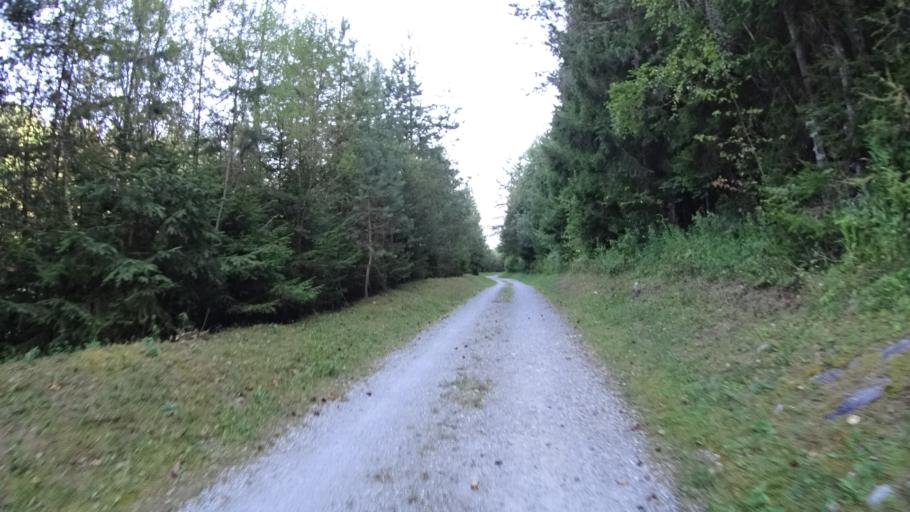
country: AT
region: Carinthia
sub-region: Politischer Bezirk Villach Land
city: Rosegg
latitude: 46.5789
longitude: 14.0190
